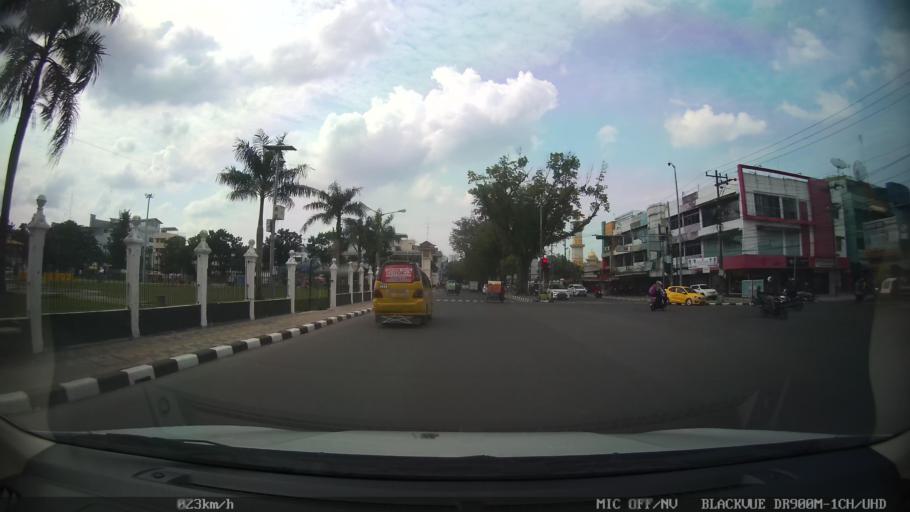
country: ID
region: North Sumatra
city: Medan
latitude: 3.5747
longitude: 98.6851
